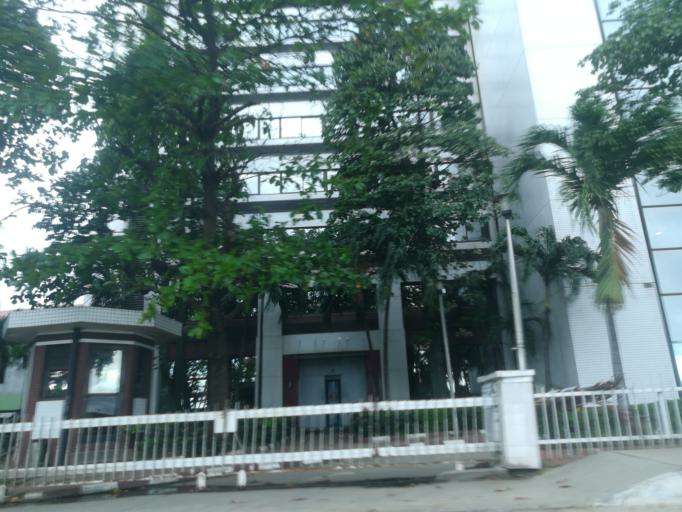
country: NG
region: Lagos
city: Lagos
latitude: 6.4487
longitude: 3.3933
